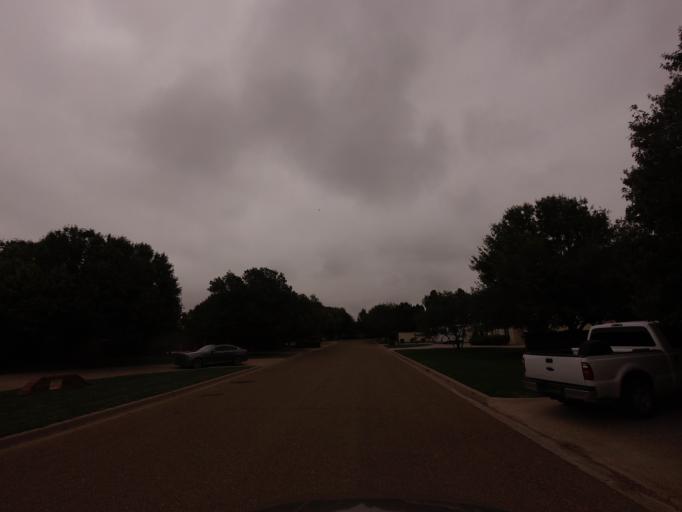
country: US
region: New Mexico
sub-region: Curry County
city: Clovis
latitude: 34.4297
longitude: -103.1817
